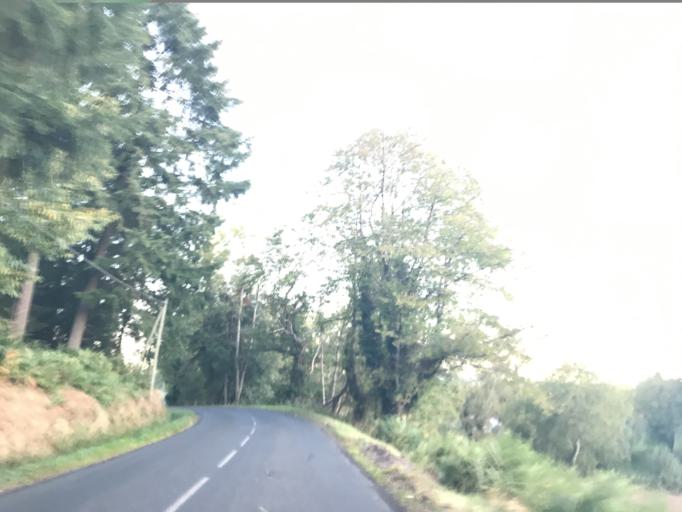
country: FR
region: Auvergne
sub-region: Departement du Puy-de-Dome
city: Celles-sur-Durolle
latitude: 45.8494
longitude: 3.6346
